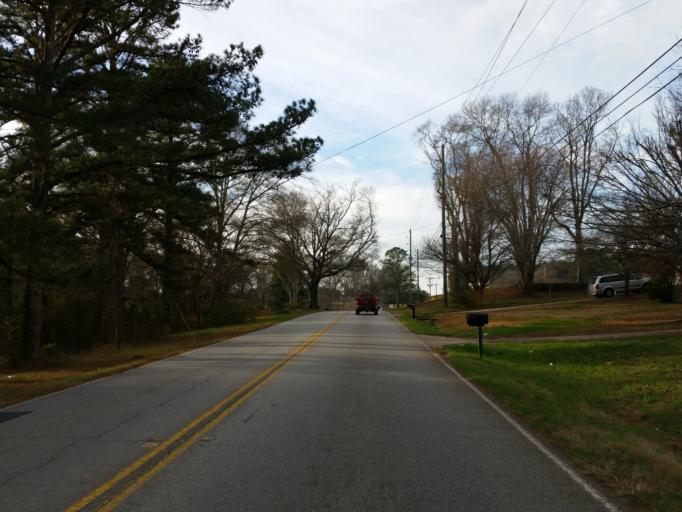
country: US
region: Georgia
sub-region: Paulding County
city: Hiram
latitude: 33.9111
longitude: -84.7592
